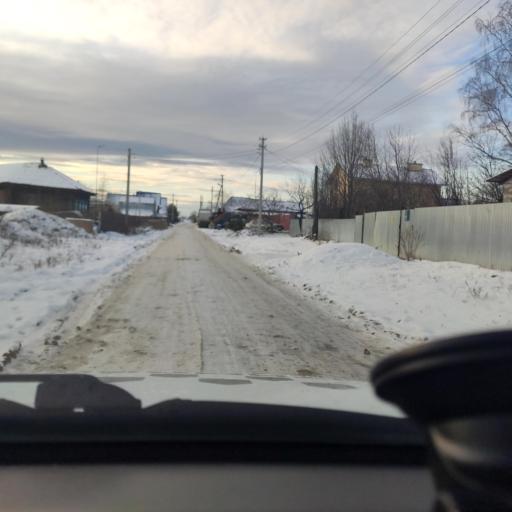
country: RU
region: Perm
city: Ferma
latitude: 57.9387
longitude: 56.3470
